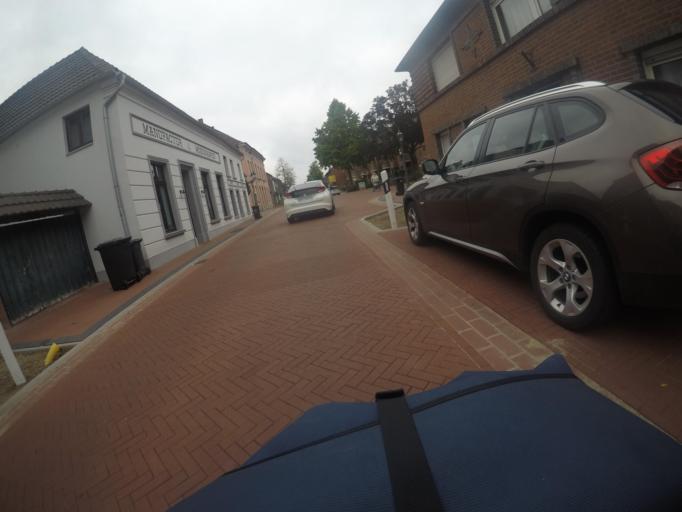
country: DE
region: North Rhine-Westphalia
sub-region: Regierungsbezirk Dusseldorf
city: Wachtendonk
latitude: 51.4575
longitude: 6.3721
